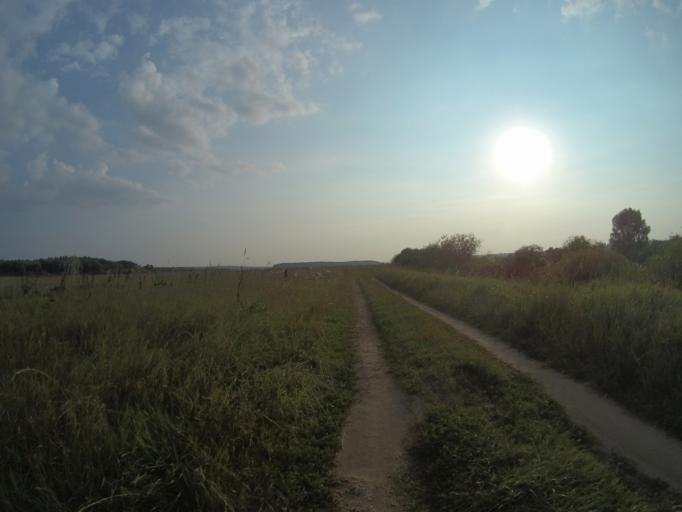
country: RU
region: Vladimir
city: Orgtrud
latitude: 56.3042
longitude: 40.6404
